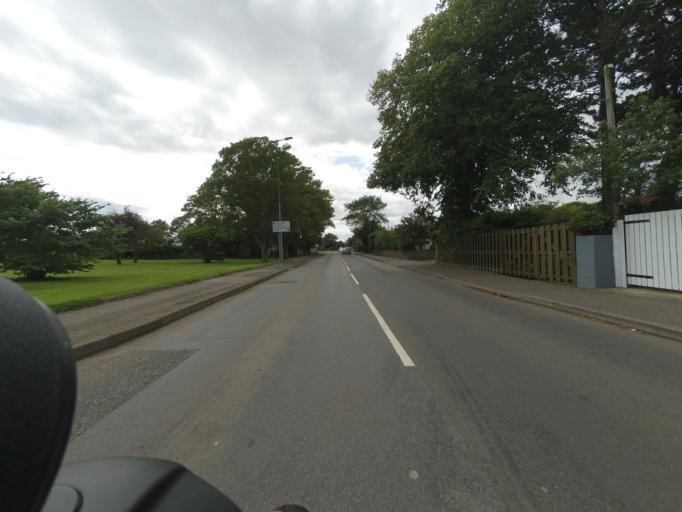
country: GB
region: Scotland
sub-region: Angus
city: Montrose
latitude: 56.7278
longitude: -2.4631
